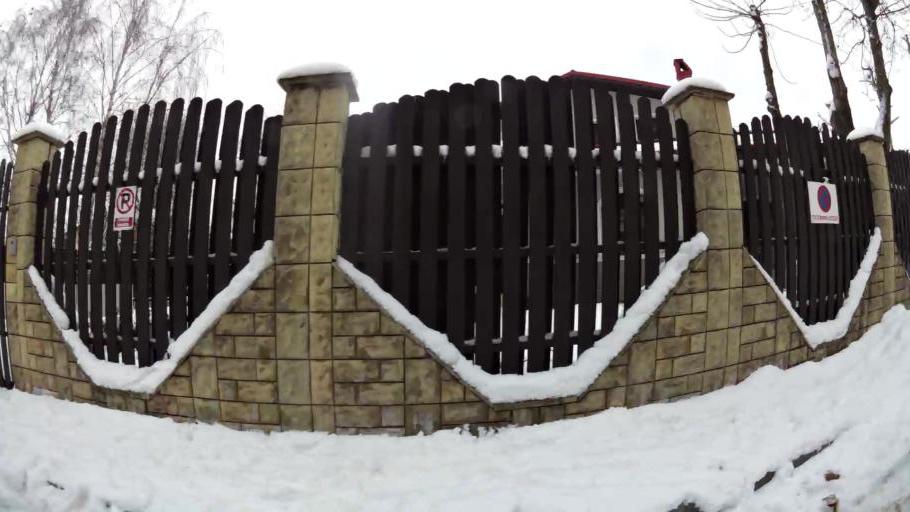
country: RO
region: Ilfov
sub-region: Comuna Otopeni
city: Otopeni
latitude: 44.5122
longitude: 26.1035
